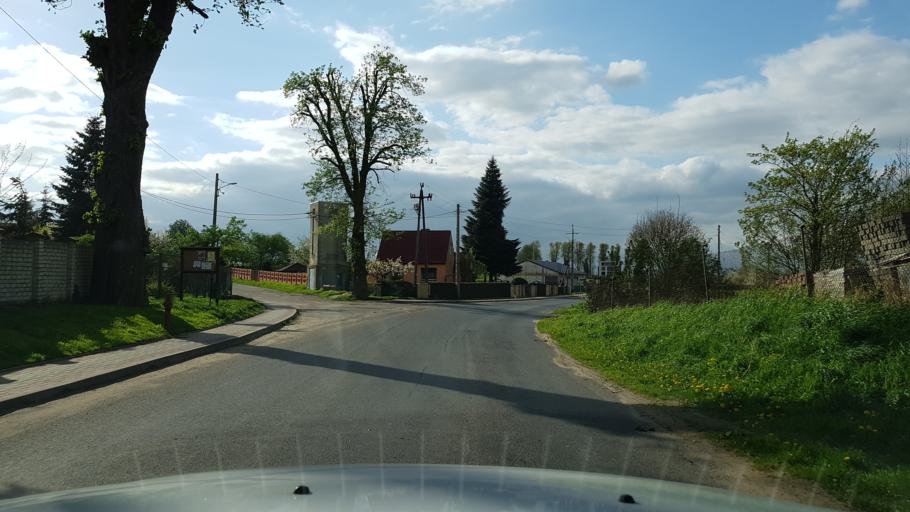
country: PL
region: West Pomeranian Voivodeship
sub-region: Powiat pyrzycki
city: Przelewice
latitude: 53.1062
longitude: 15.0727
